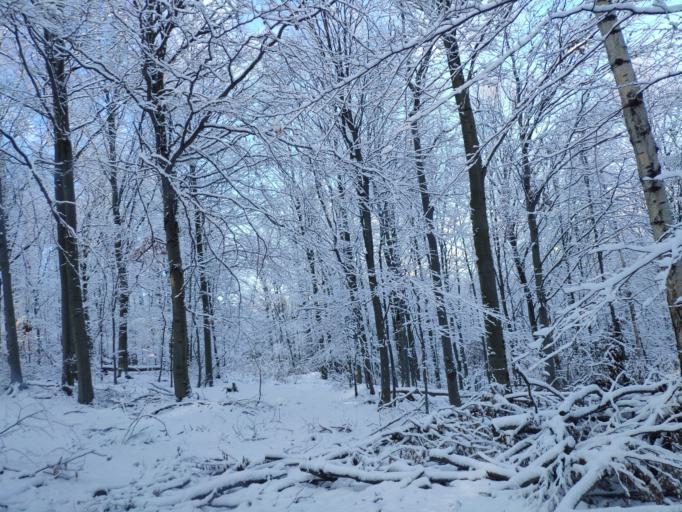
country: SK
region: Kosicky
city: Moldava nad Bodvou
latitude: 48.7489
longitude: 21.0829
